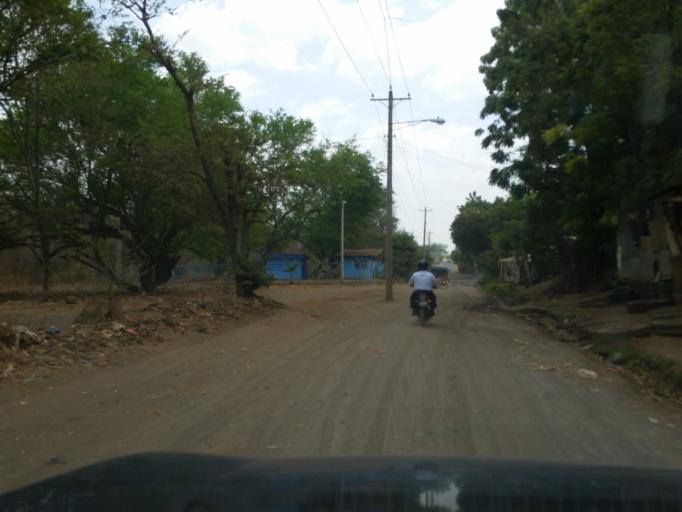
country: NI
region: Managua
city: Managua
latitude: 12.1370
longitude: -86.1869
